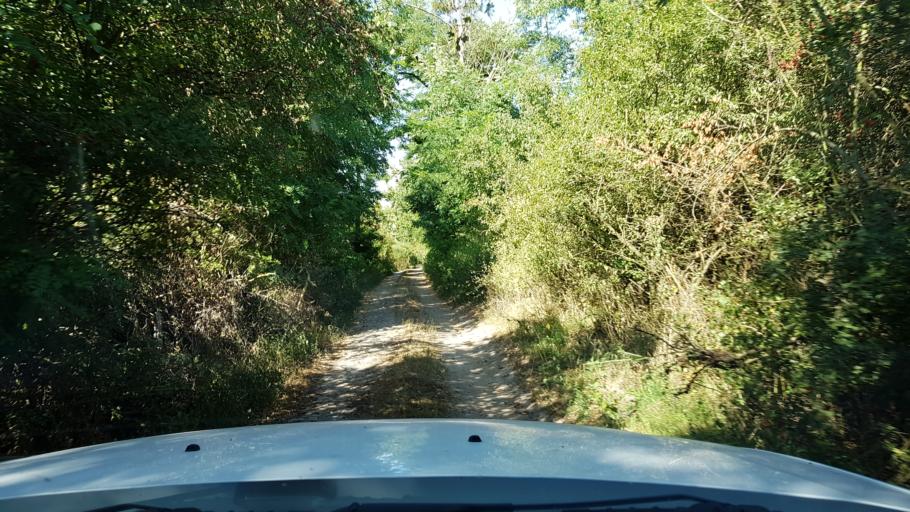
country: PL
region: West Pomeranian Voivodeship
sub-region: Powiat gryfinski
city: Cedynia
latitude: 52.8539
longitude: 14.2268
